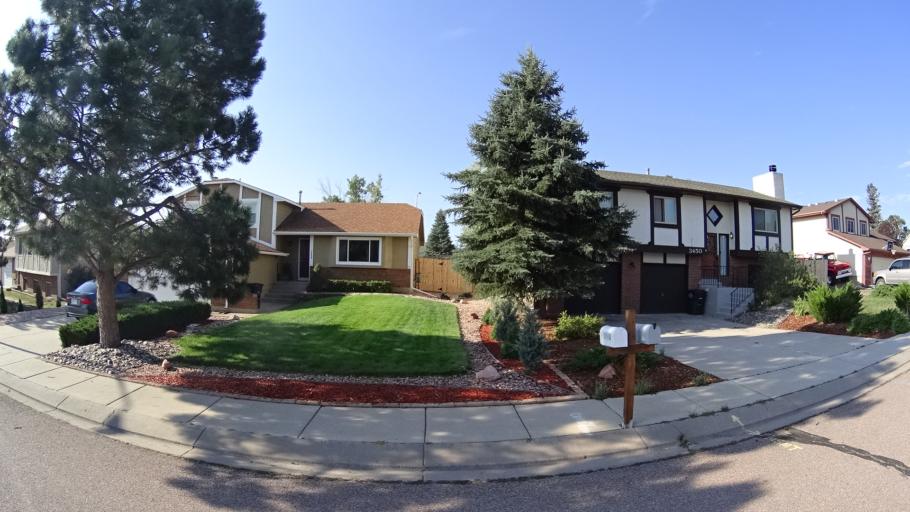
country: US
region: Colorado
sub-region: El Paso County
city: Black Forest
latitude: 38.9423
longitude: -104.7644
